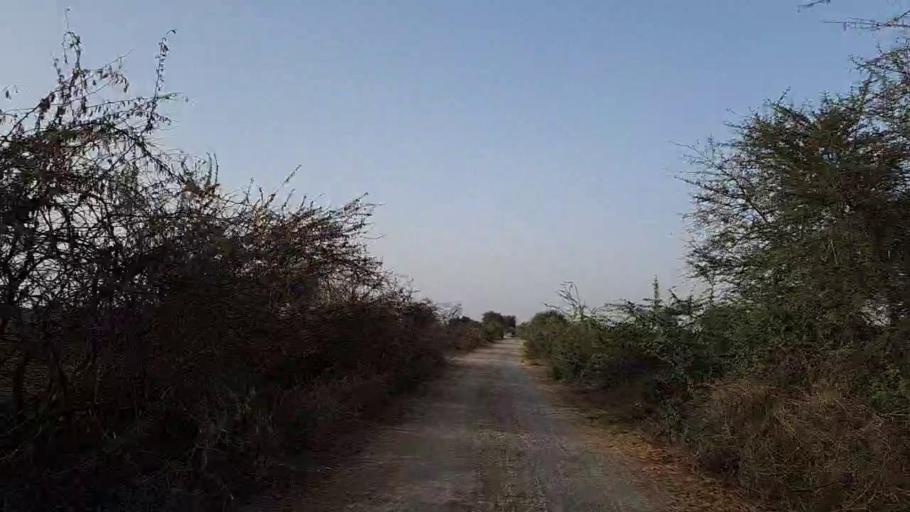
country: PK
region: Sindh
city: Jati
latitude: 24.4084
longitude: 68.1858
